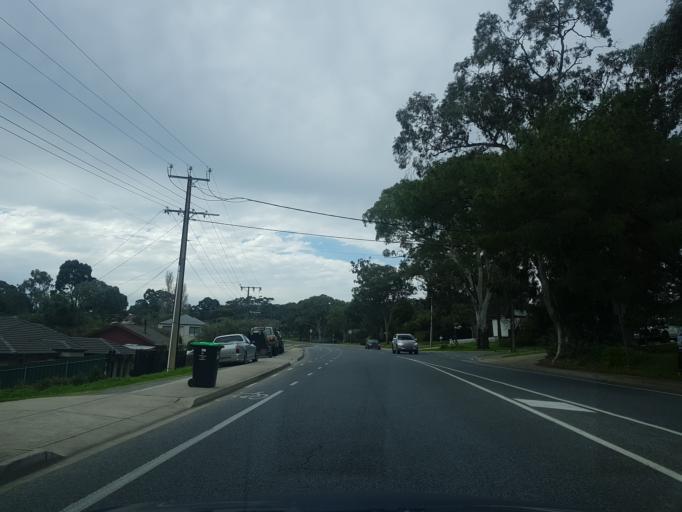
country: AU
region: South Australia
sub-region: Tea Tree Gully
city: Hope Valley
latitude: -34.8498
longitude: 138.7146
